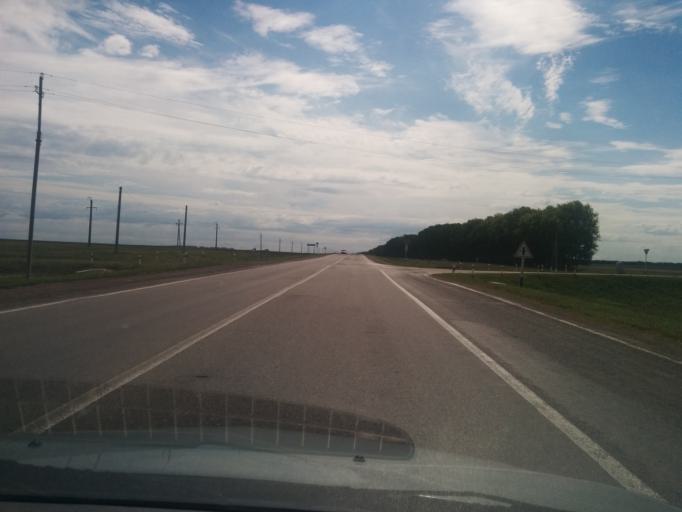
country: RU
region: Bashkortostan
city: Karmaskaly
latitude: 54.4208
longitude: 56.0438
